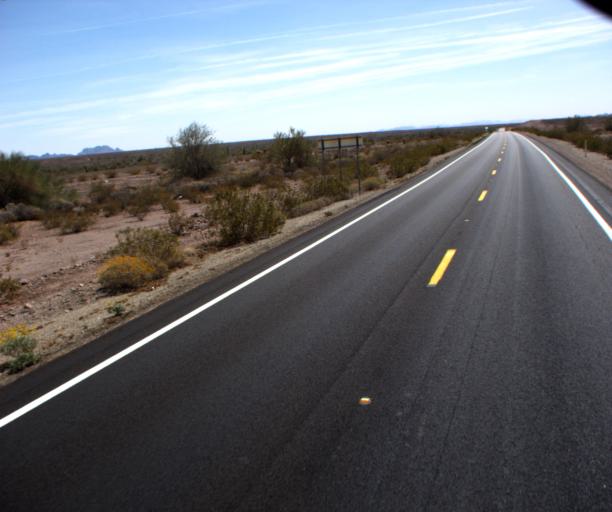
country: US
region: Arizona
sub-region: La Paz County
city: Quartzsite
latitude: 33.1839
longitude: -114.2753
